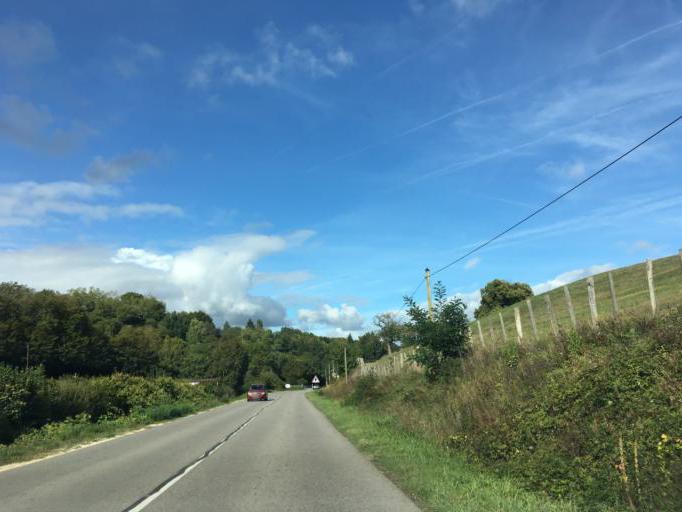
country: FR
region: Rhone-Alpes
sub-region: Departement de l'Isere
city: Saint-Didier-de-la-Tour
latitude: 45.5632
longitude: 5.4758
